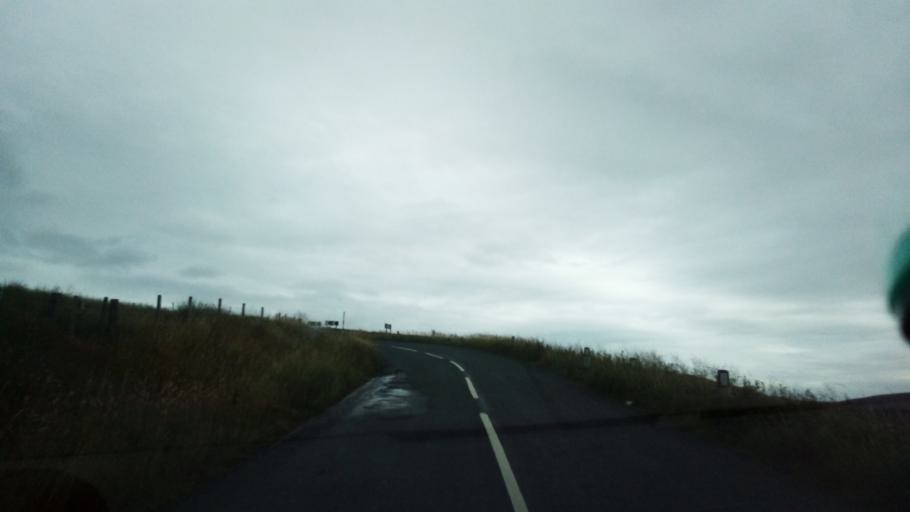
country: GB
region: England
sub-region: County Durham
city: Holwick
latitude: 54.5904
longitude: -2.1781
